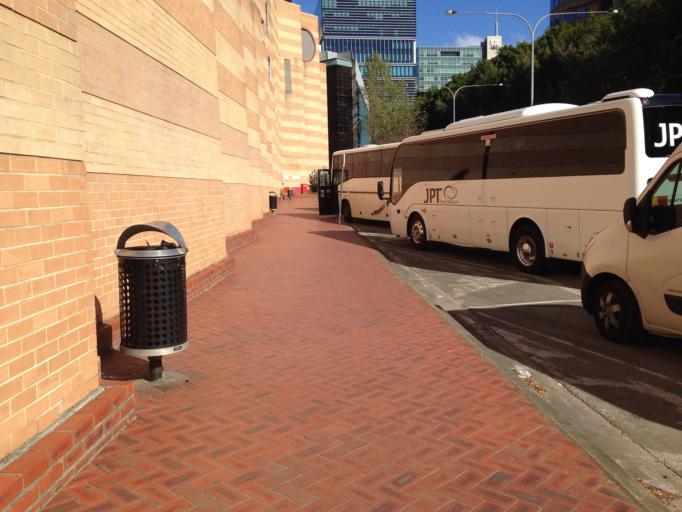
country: AU
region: New South Wales
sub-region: City of Sydney
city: Haymarket
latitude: -33.8796
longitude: 151.2014
